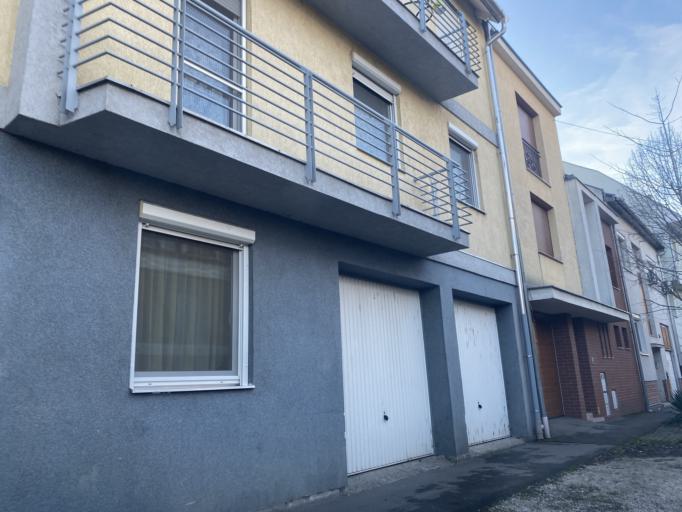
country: HU
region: Csongrad
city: Szeged
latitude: 46.2619
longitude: 20.1424
